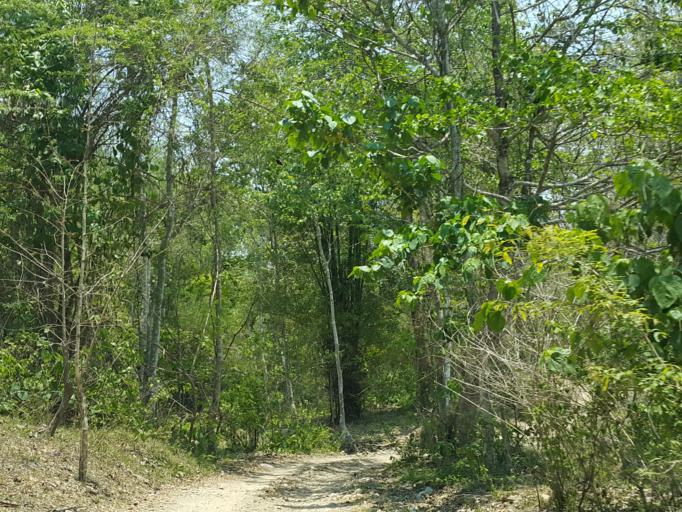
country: TH
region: Kanchanaburi
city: Sai Yok
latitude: 14.2326
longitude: 98.8558
